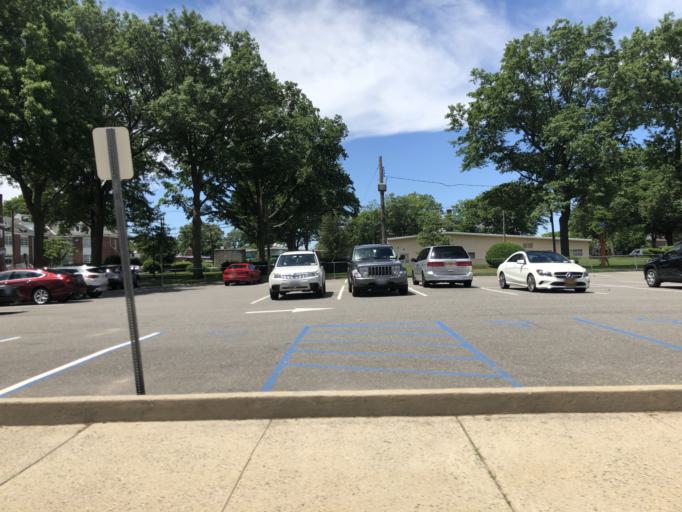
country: US
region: New York
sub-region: Nassau County
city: East Garden City
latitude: 40.7301
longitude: -73.5967
